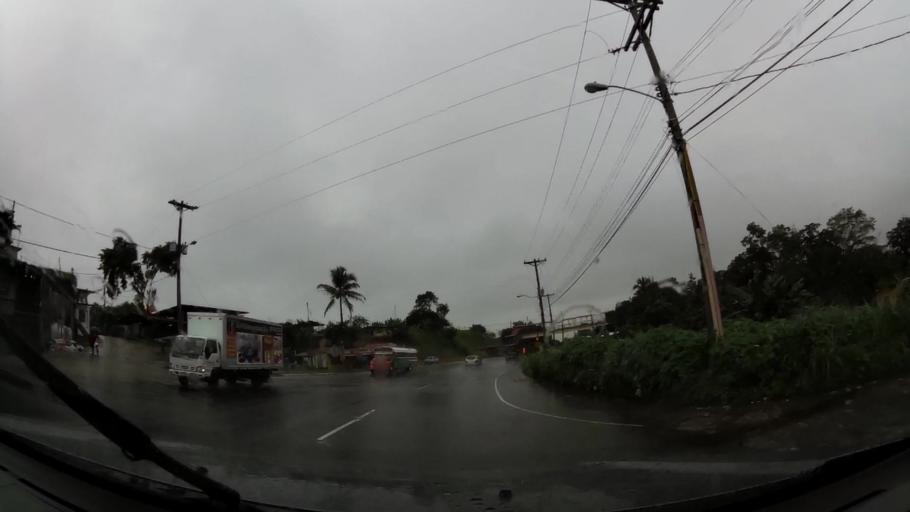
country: PA
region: Colon
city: Santa Rita Arriba
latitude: 9.3331
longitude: -79.8041
